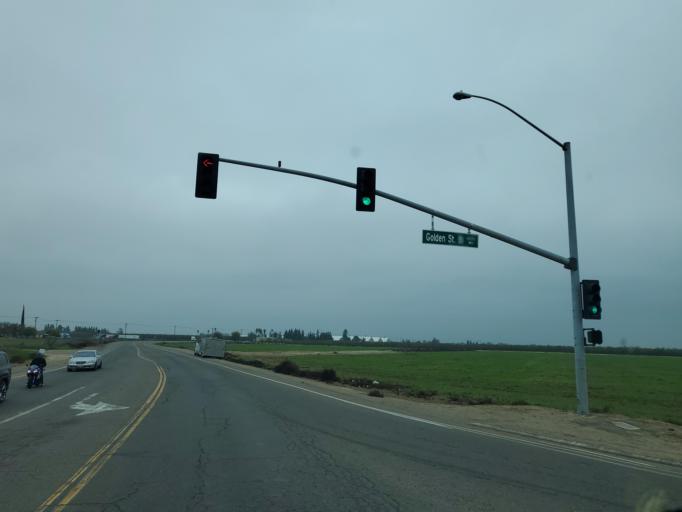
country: US
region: California
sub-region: Stanislaus County
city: Keyes
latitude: 37.5489
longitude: -120.9018
